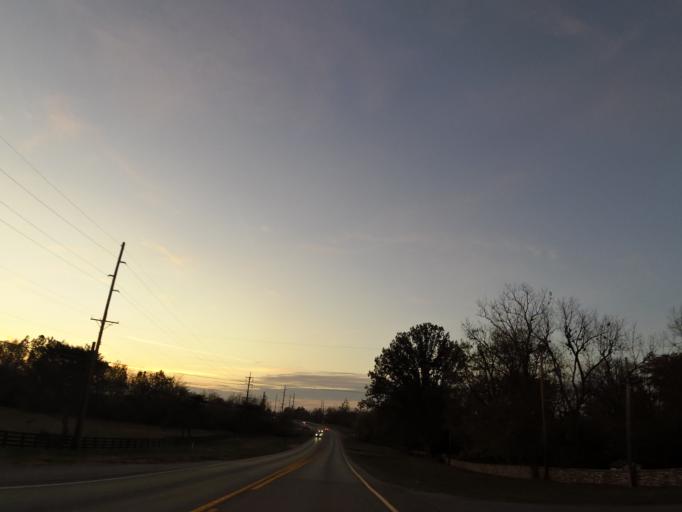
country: US
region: Kentucky
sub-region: Fayette County
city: Lexington-Fayette
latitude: 38.0392
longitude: -84.4083
